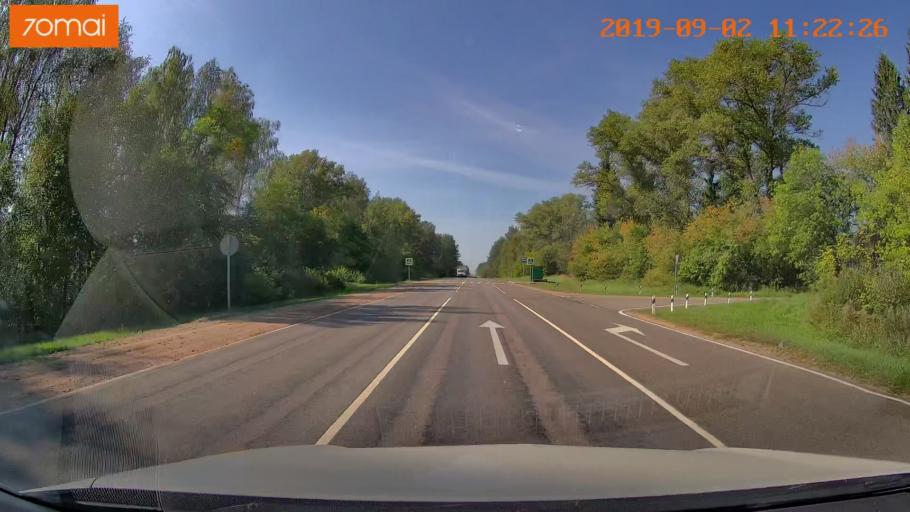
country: RU
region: Smolensk
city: Roslavl'
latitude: 54.0260
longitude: 33.0138
